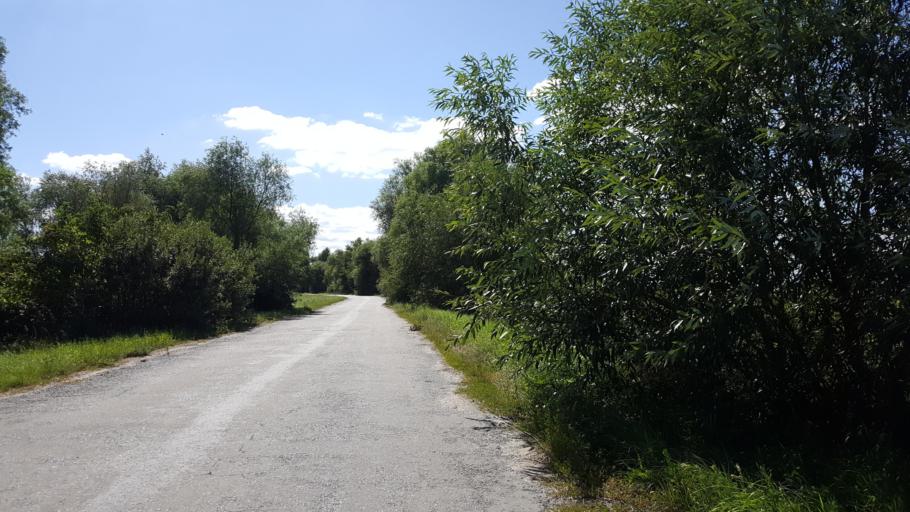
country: BY
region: Brest
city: Kobryn
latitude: 52.3149
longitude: 24.2981
